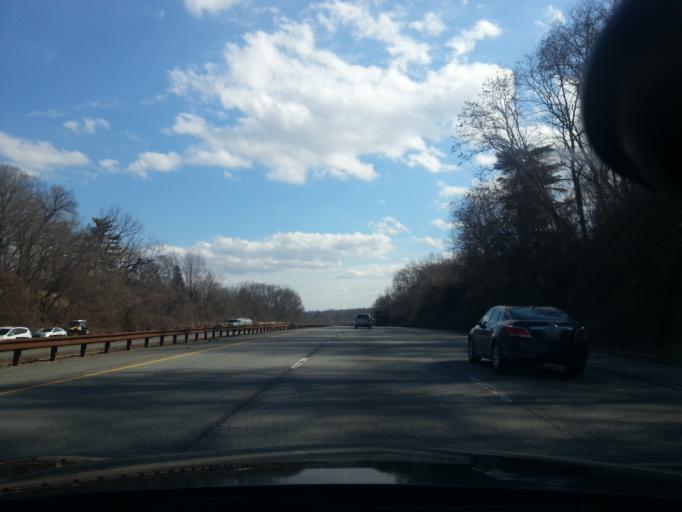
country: US
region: Pennsylvania
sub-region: Delaware County
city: Broomall
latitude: 40.0132
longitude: -75.3569
